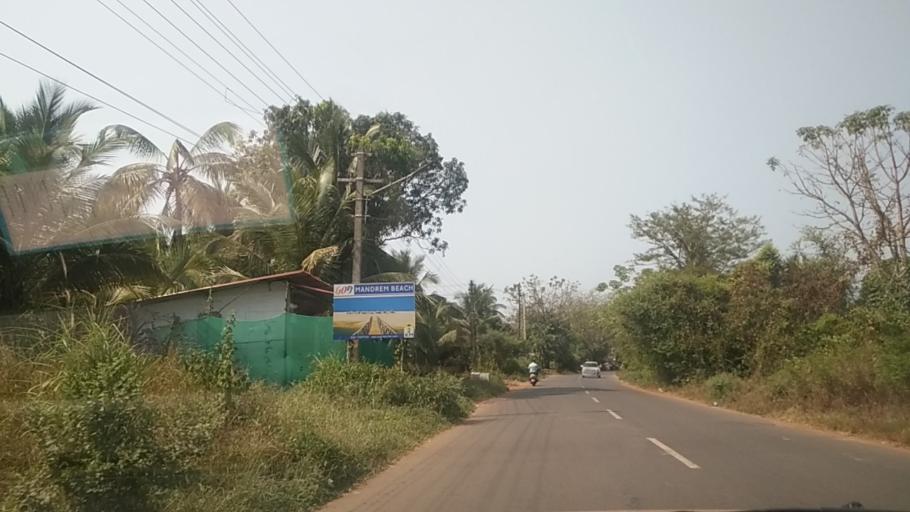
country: IN
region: Goa
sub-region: North Goa
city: Arambol
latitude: 15.6640
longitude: 73.7251
